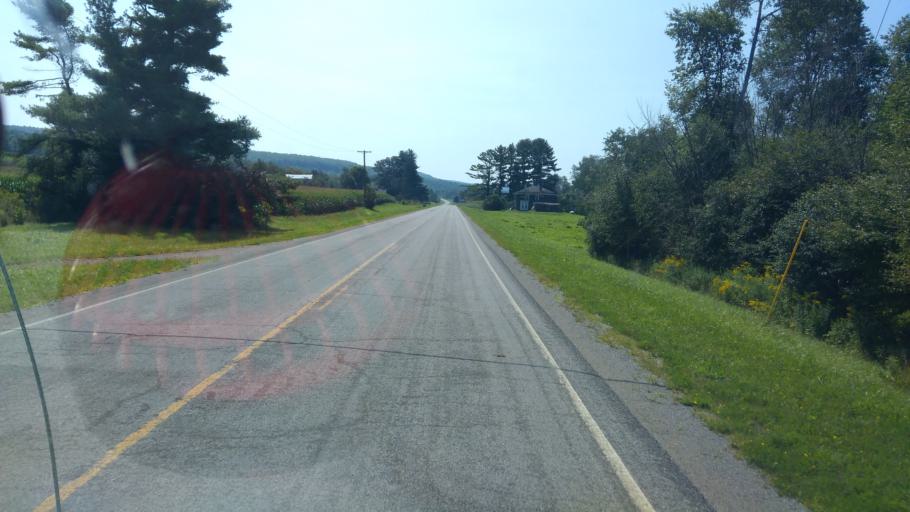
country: US
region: New York
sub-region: Allegany County
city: Belmont
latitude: 42.3454
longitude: -77.9275
